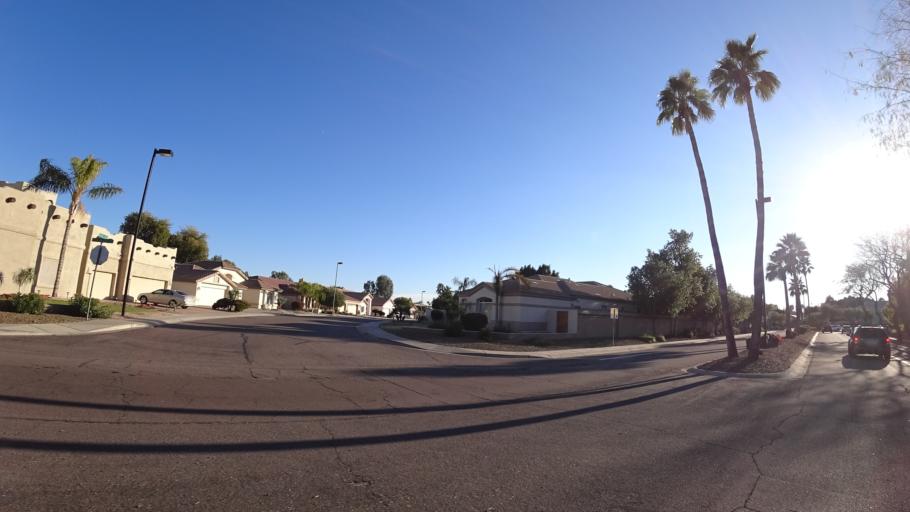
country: US
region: Arizona
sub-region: Maricopa County
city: Peoria
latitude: 33.6824
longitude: -112.1906
